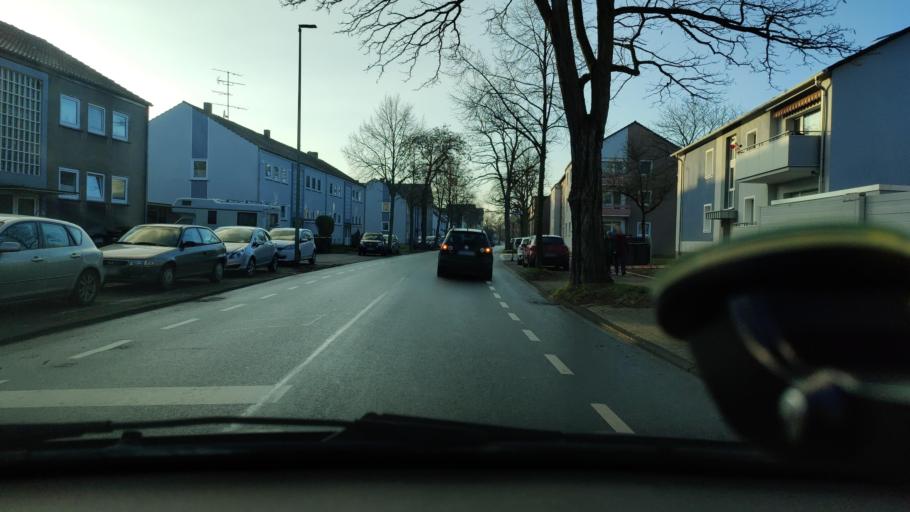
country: DE
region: North Rhine-Westphalia
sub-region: Regierungsbezirk Dusseldorf
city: Dinslaken
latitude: 51.5330
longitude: 6.7084
